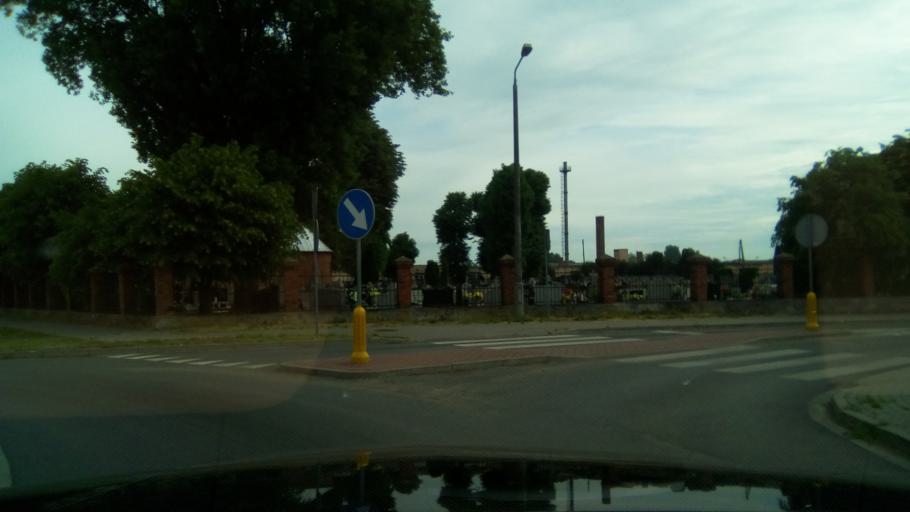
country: PL
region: Kujawsko-Pomorskie
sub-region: Powiat zninski
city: Janowiec Wielkopolski
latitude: 52.7498
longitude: 17.4885
